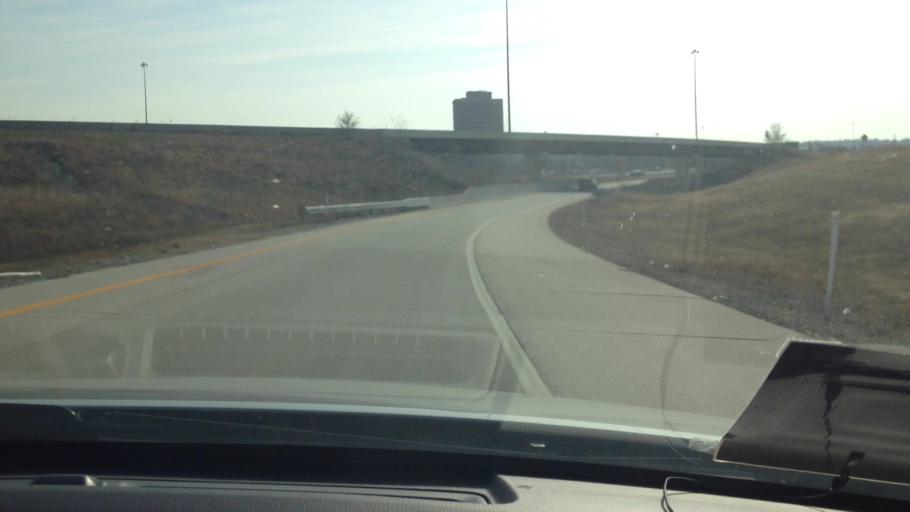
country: US
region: Kansas
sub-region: Johnson County
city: Lenexa
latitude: 38.9331
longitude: -94.7073
